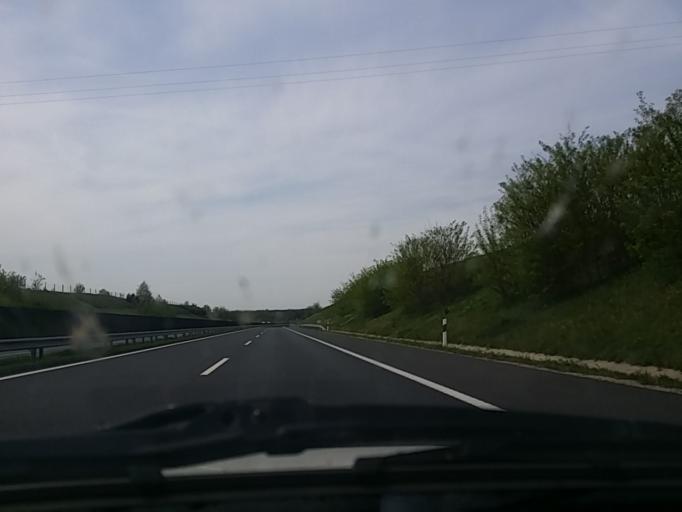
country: HU
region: Zala
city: Nagykanizsa
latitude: 46.4818
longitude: 17.0847
